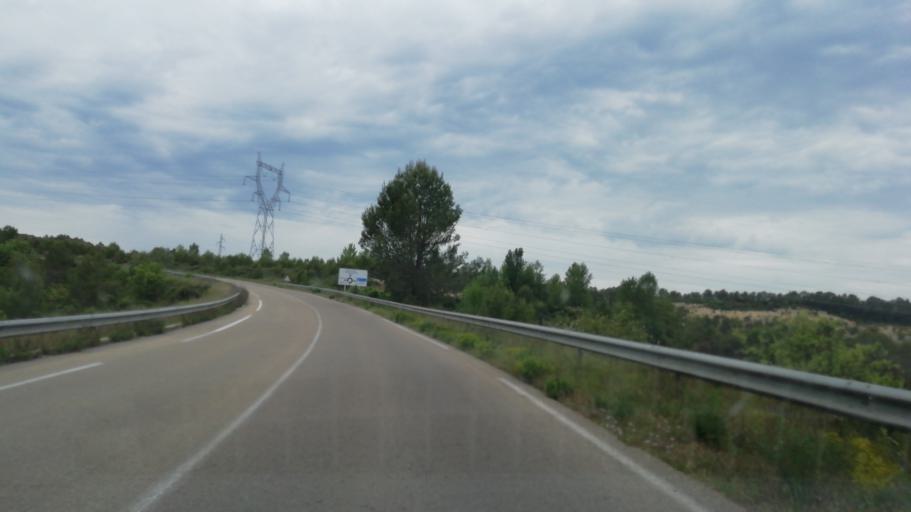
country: FR
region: Languedoc-Roussillon
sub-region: Departement de l'Herault
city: Les Matelles
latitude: 43.7089
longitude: 3.8223
